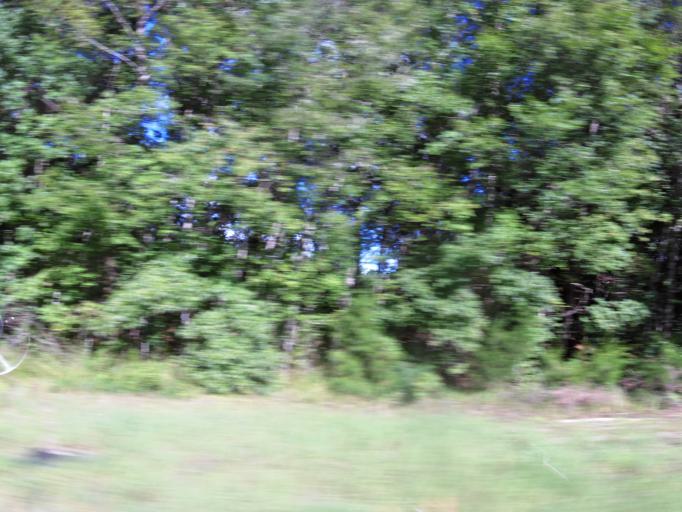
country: US
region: Georgia
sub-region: Camden County
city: Woodbine
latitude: 31.0832
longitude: -81.7265
